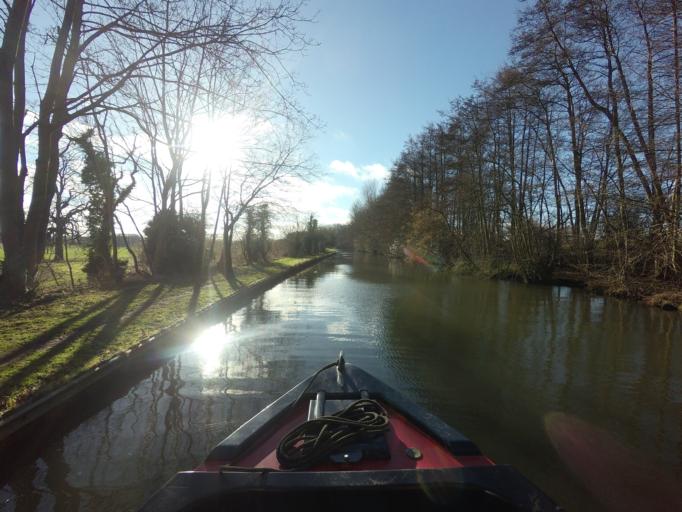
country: GB
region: England
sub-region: Northamptonshire
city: Long Buckby
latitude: 52.2575
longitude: -1.0846
